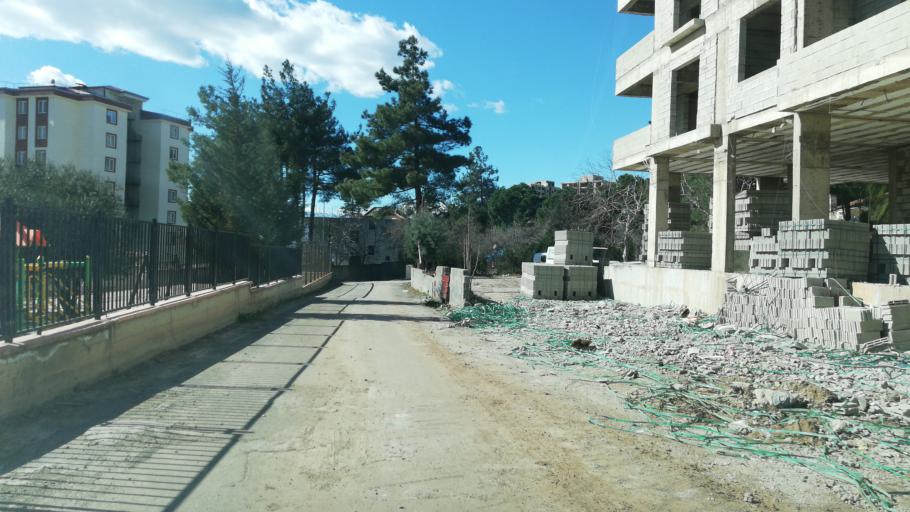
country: TR
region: Kahramanmaras
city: Kahramanmaras
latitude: 37.6008
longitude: 36.8253
